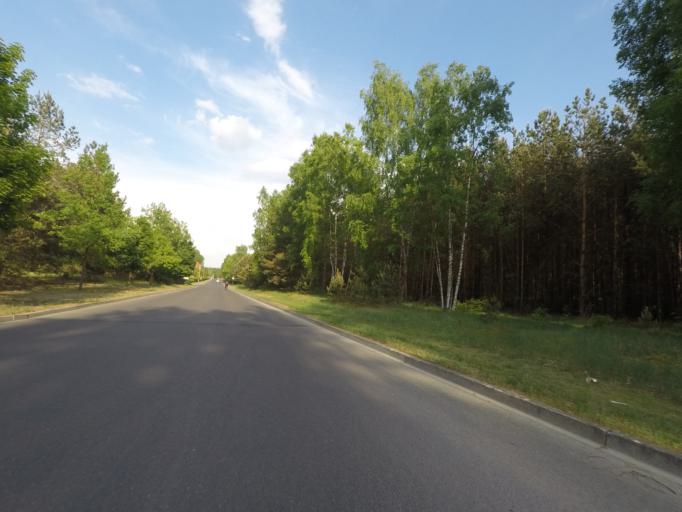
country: DE
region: Brandenburg
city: Eberswalde
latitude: 52.8280
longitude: 13.7578
